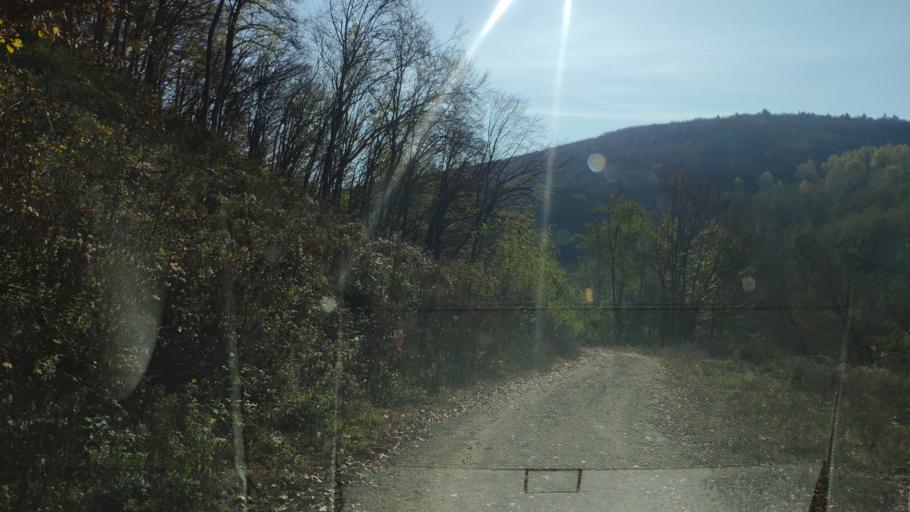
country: SK
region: Presovsky
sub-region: Okres Presov
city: Presov
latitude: 48.9033
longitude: 21.2251
